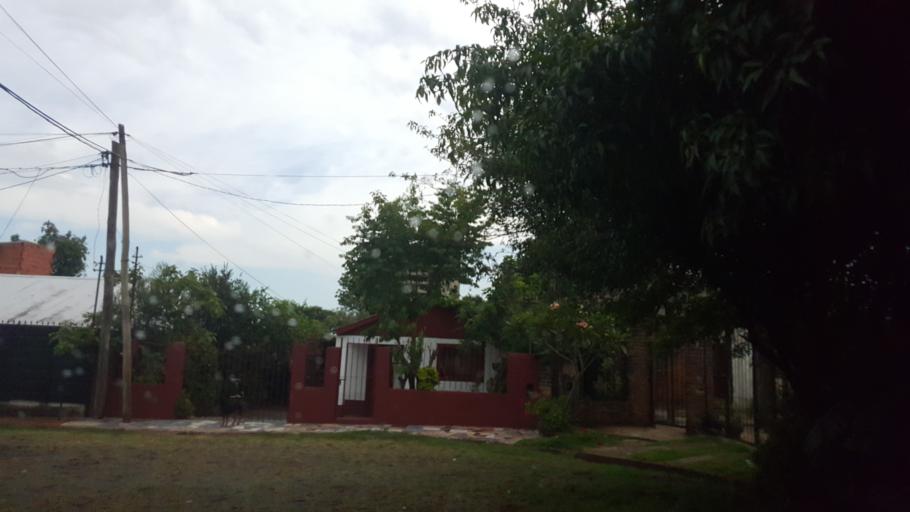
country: AR
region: Misiones
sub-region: Departamento de Capital
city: Posadas
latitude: -27.3898
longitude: -55.8949
